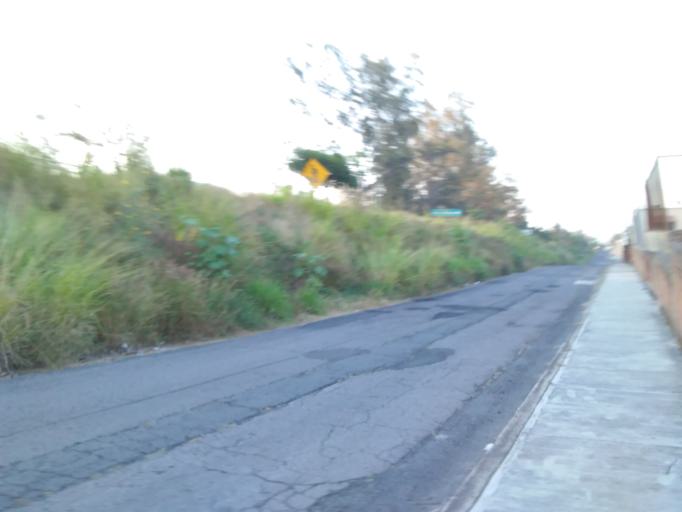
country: MX
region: Nayarit
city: Tepic
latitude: 21.5133
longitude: -104.9239
